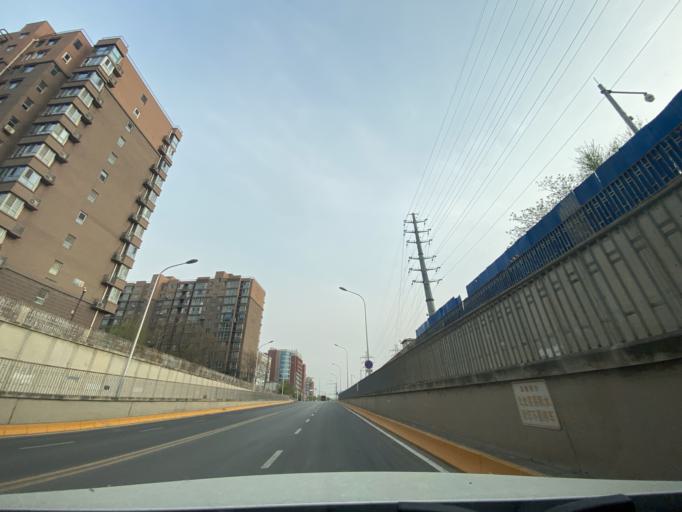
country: CN
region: Beijing
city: Babaoshan
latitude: 39.9302
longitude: 116.2327
